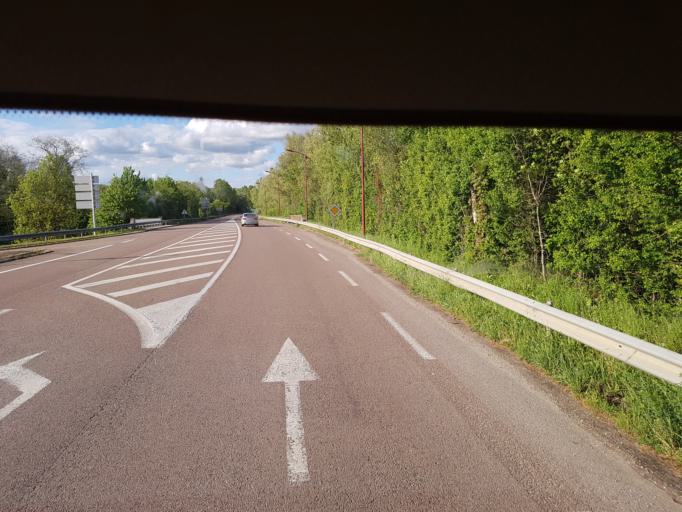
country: FR
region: Bourgogne
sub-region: Departement de l'Yonne
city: Saint-Florentin
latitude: 47.9965
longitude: 3.7353
